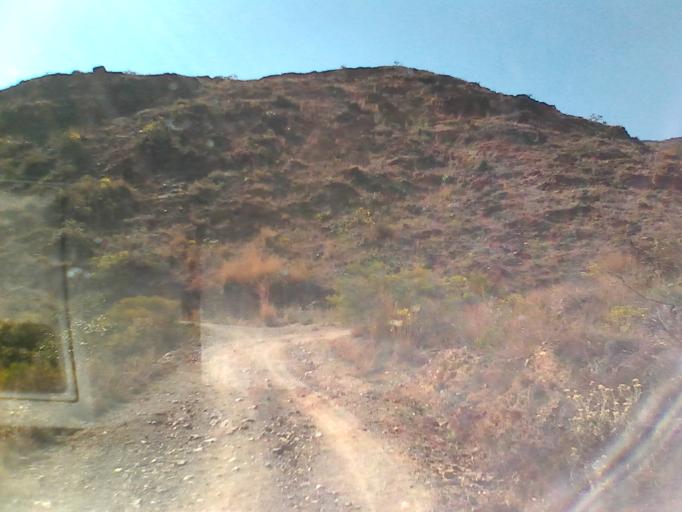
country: CO
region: Boyaca
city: Sachica
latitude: 5.5547
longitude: -73.5474
